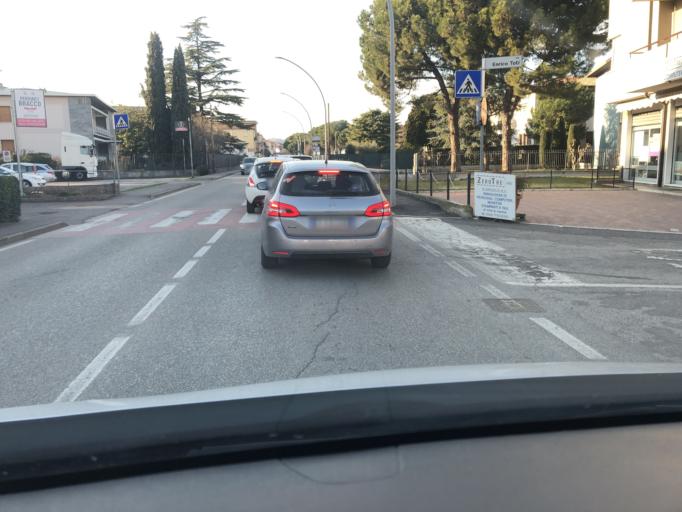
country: IT
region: Veneto
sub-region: Provincia di Verona
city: Bussolengo
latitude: 45.4688
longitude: 10.8478
